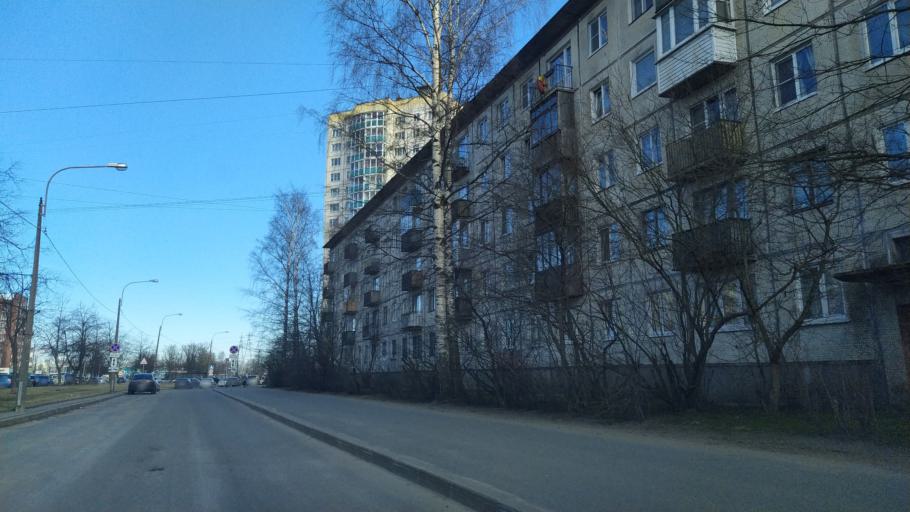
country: RU
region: Leningrad
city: Akademicheskoe
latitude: 60.0109
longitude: 30.4285
